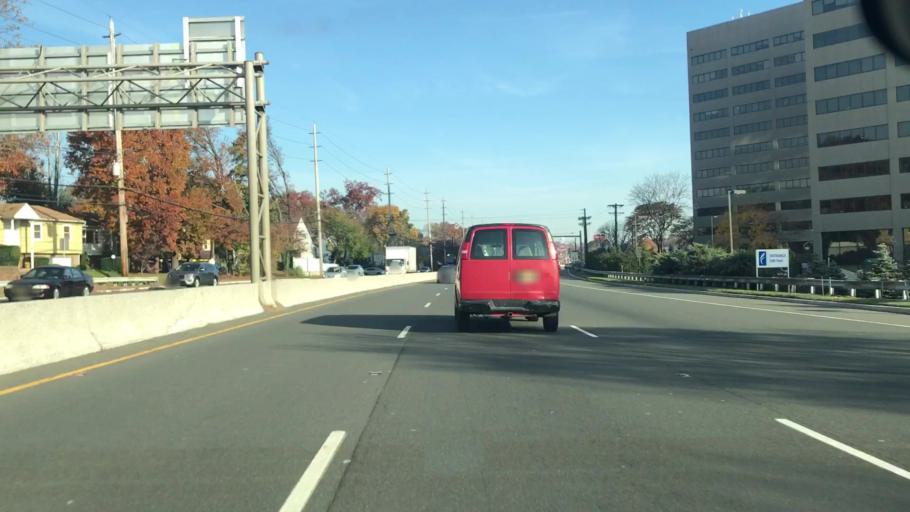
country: US
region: New Jersey
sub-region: Bergen County
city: Rutherford
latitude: 40.8165
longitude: -74.1026
